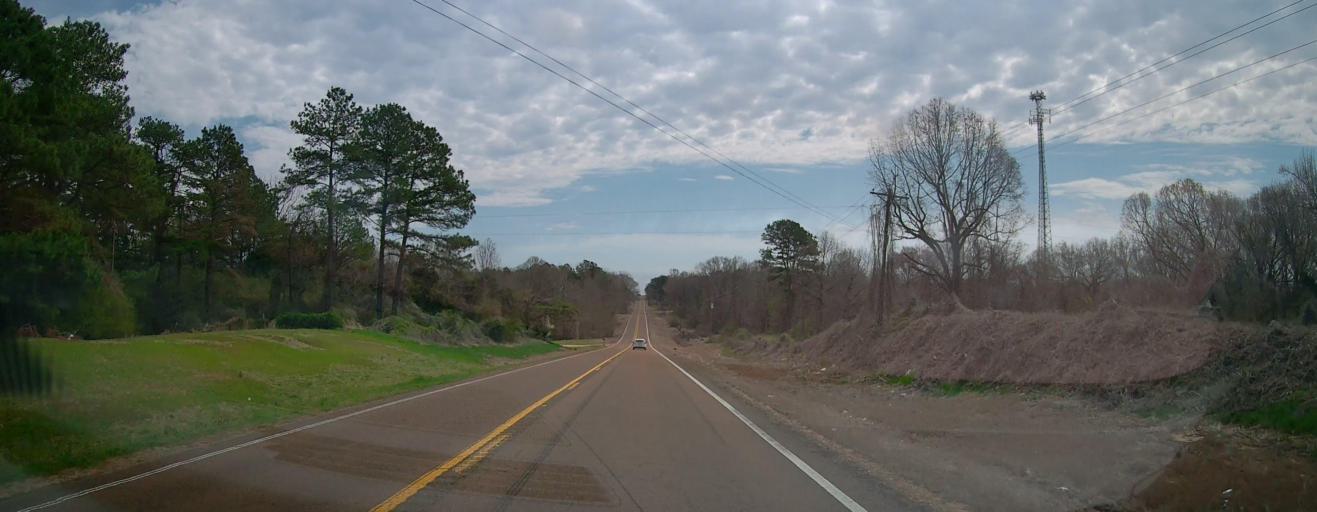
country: US
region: Mississippi
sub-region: Marshall County
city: Holly Springs
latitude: 34.8209
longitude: -89.5436
